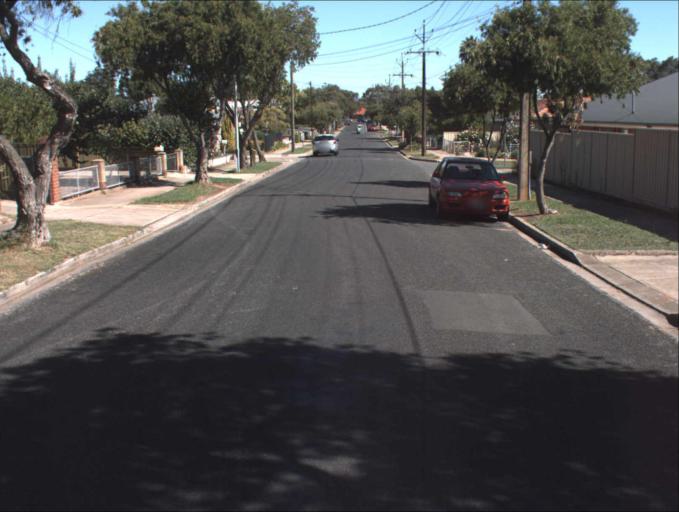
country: AU
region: South Australia
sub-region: Port Adelaide Enfield
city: Blair Athol
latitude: -34.8707
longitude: 138.6132
